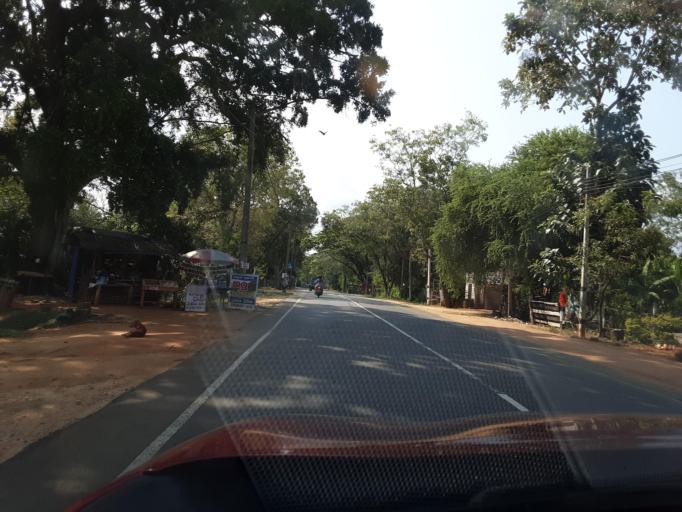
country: LK
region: Uva
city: Haputale
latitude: 6.3511
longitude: 81.1946
